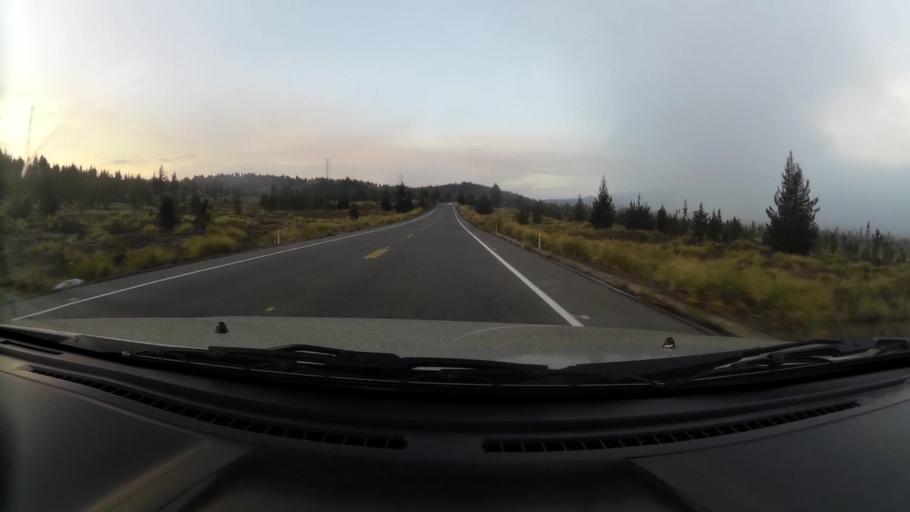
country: EC
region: Chimborazo
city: Alausi
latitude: -2.0516
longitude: -78.7427
